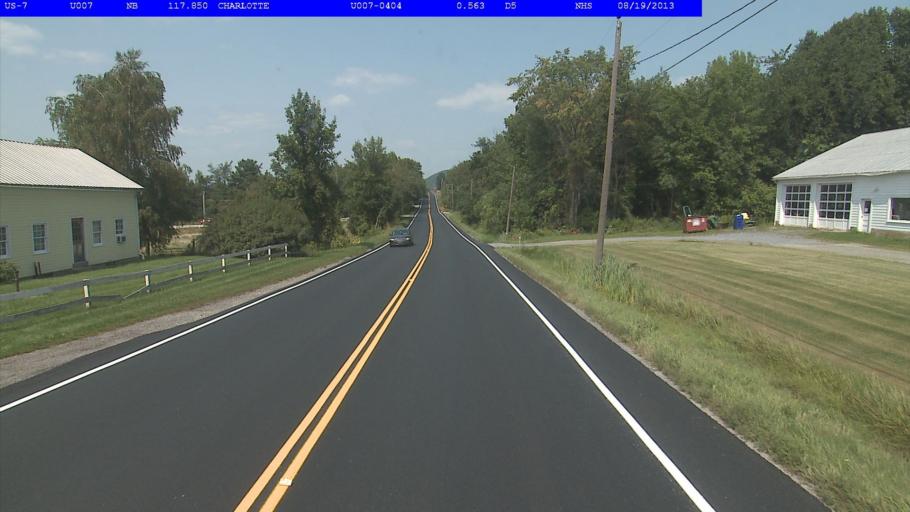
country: US
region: Vermont
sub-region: Addison County
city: Vergennes
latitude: 44.2703
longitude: -73.2333
